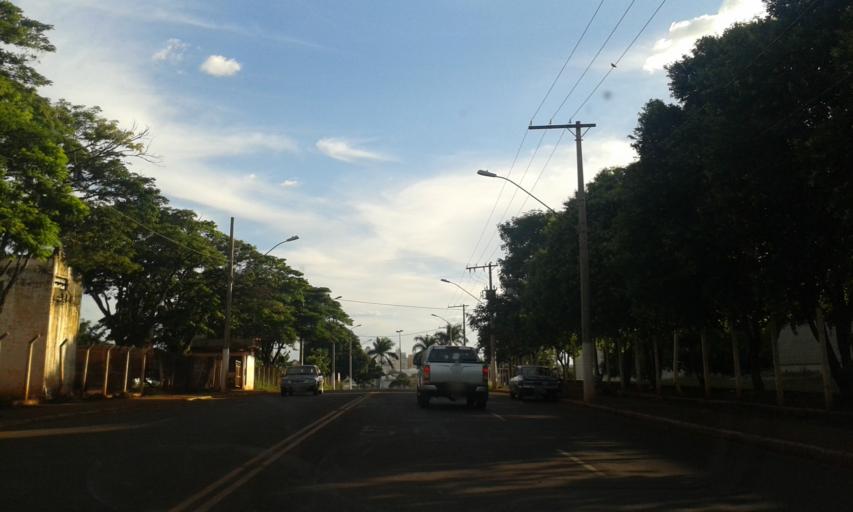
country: BR
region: Minas Gerais
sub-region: Ituiutaba
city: Ituiutaba
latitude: -18.9594
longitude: -49.4574
